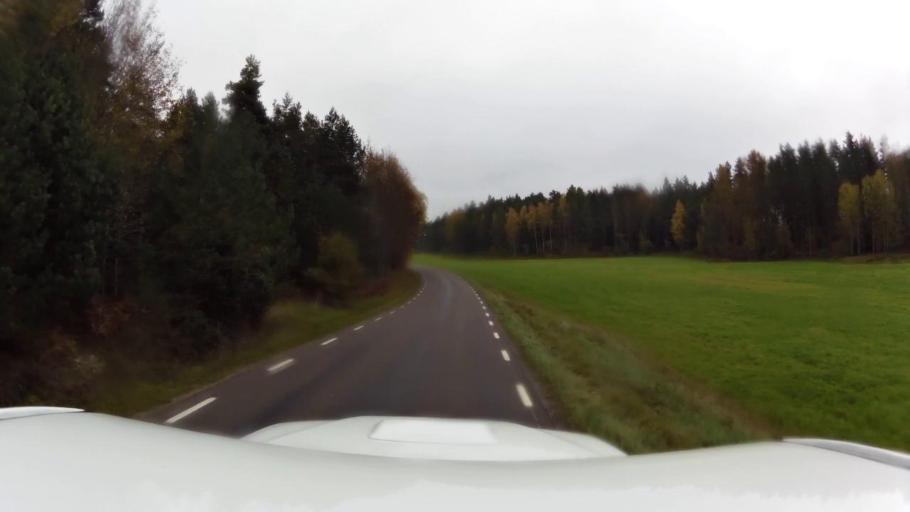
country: SE
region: OEstergoetland
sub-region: Linkopings Kommun
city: Linghem
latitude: 58.3530
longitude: 15.8579
